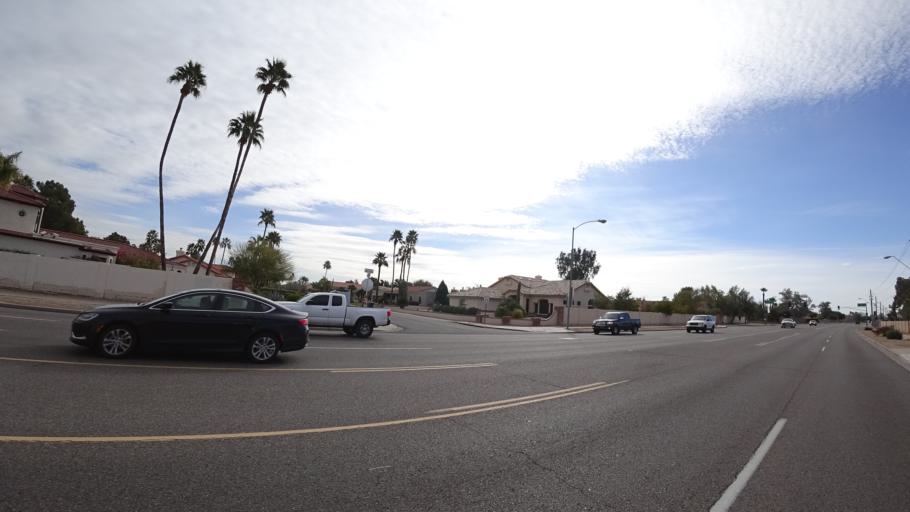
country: US
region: Arizona
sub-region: Maricopa County
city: Peoria
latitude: 33.6337
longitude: -112.1513
